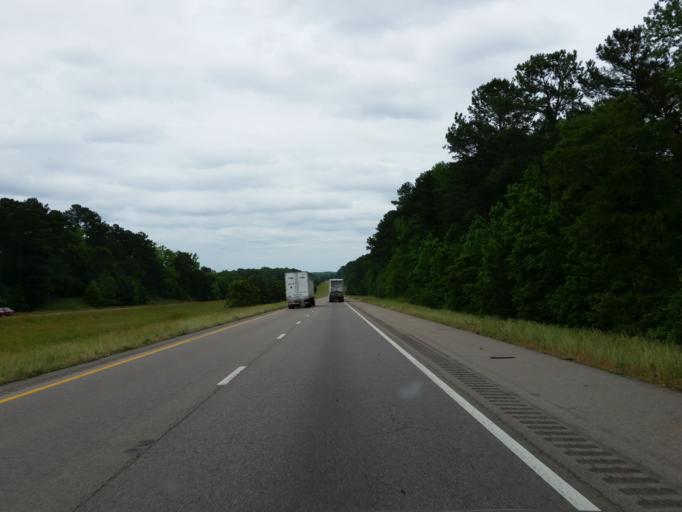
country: US
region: Mississippi
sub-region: Lauderdale County
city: Marion
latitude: 32.4067
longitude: -88.5434
